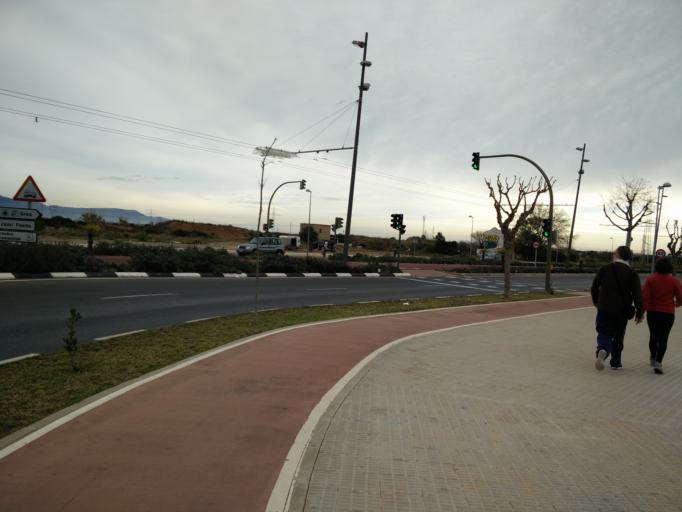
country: ES
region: Valencia
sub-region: Provincia de Castello
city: Castello de la Plana
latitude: 39.9821
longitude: -0.0173
